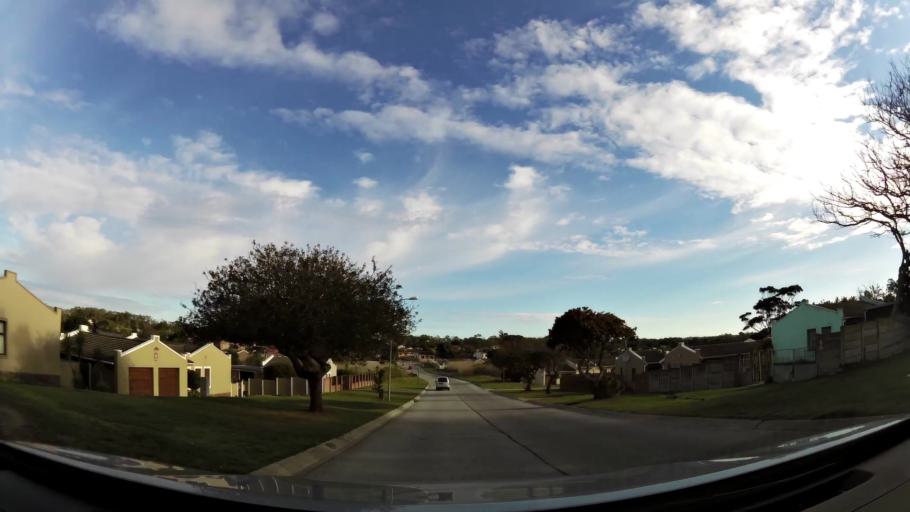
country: ZA
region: Eastern Cape
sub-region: Nelson Mandela Bay Metropolitan Municipality
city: Port Elizabeth
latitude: -33.9620
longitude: 25.4770
